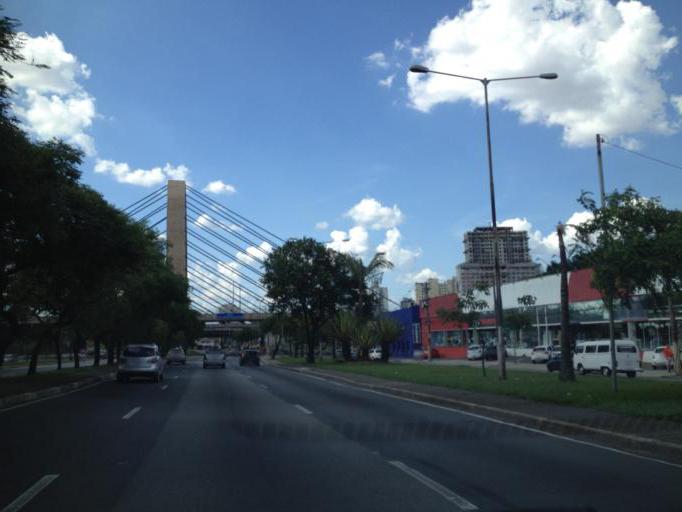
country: BR
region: Sao Paulo
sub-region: Sao Paulo
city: Sao Paulo
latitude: -23.5444
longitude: -46.5800
